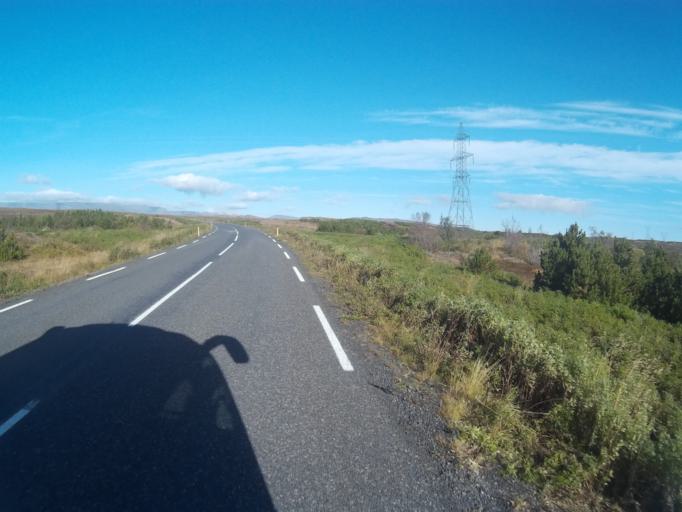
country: IS
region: Capital Region
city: Mosfellsbaer
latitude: 64.0998
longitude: -21.6896
